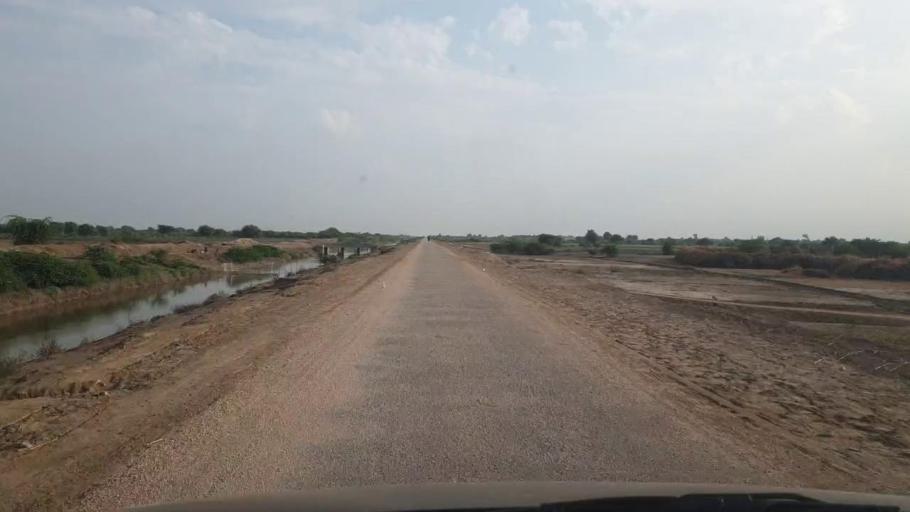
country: PK
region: Sindh
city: Badin
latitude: 24.5409
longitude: 68.6741
